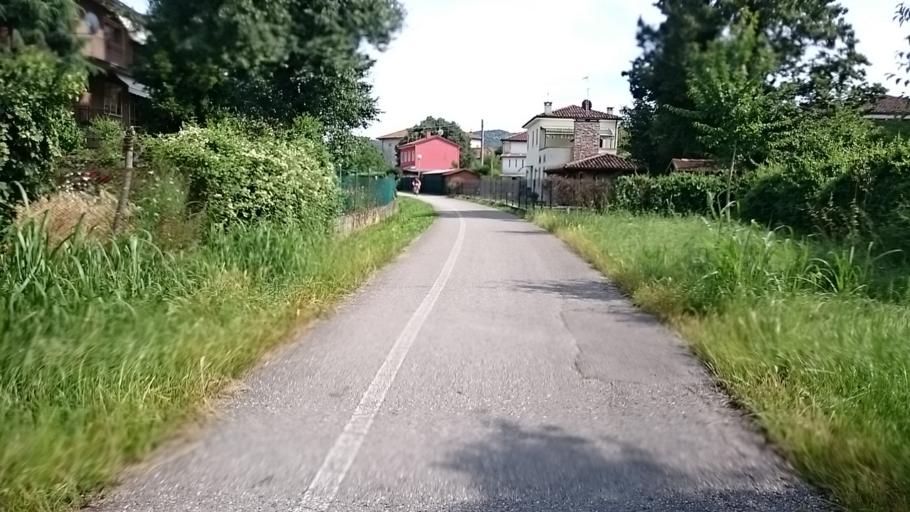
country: IT
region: Veneto
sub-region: Provincia di Vicenza
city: Arcugnano-Torri
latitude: 45.5061
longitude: 11.5703
